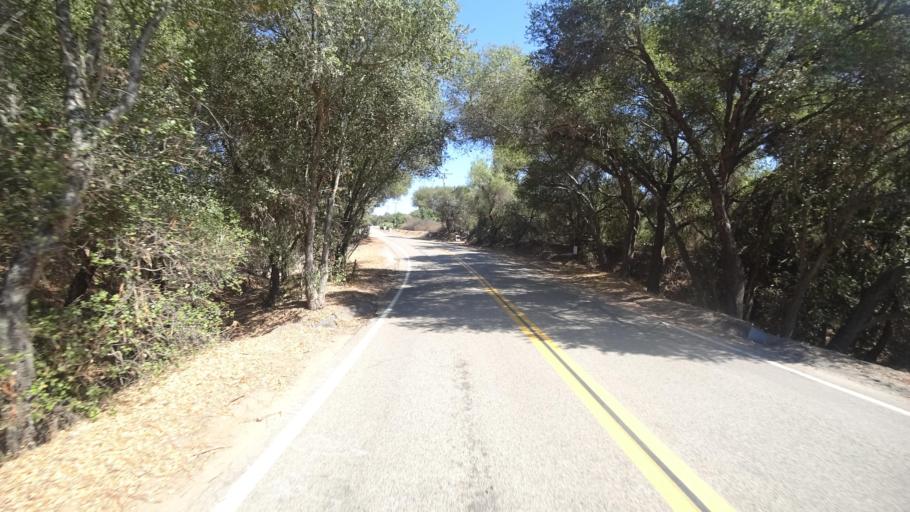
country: US
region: California
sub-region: San Diego County
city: Hidden Meadows
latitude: 33.2835
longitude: -117.1188
